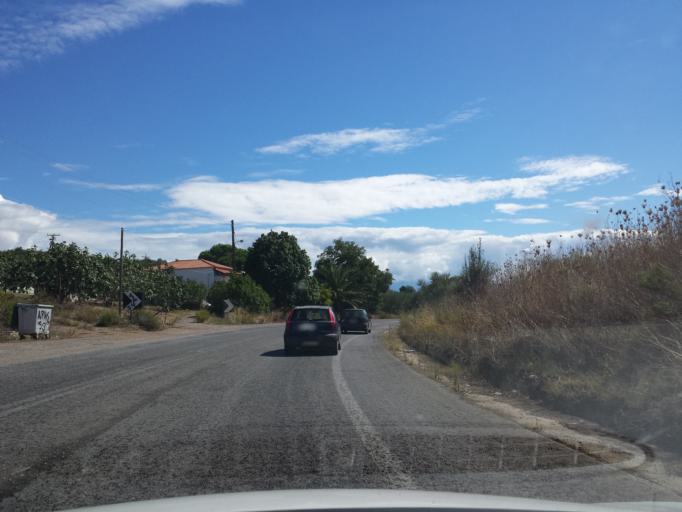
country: GR
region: Peloponnese
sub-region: Nomos Messinias
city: Vlakhopoulon
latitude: 37.0051
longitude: 21.8984
